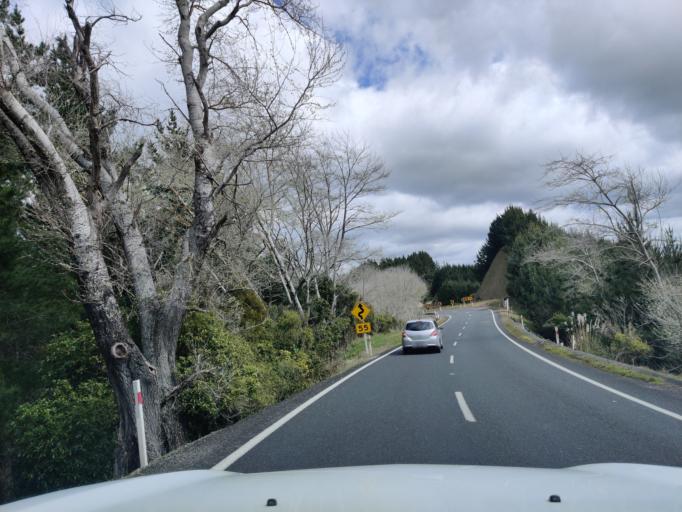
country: NZ
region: Manawatu-Wanganui
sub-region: Wanganui District
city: Wanganui
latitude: -39.7928
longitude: 175.2107
